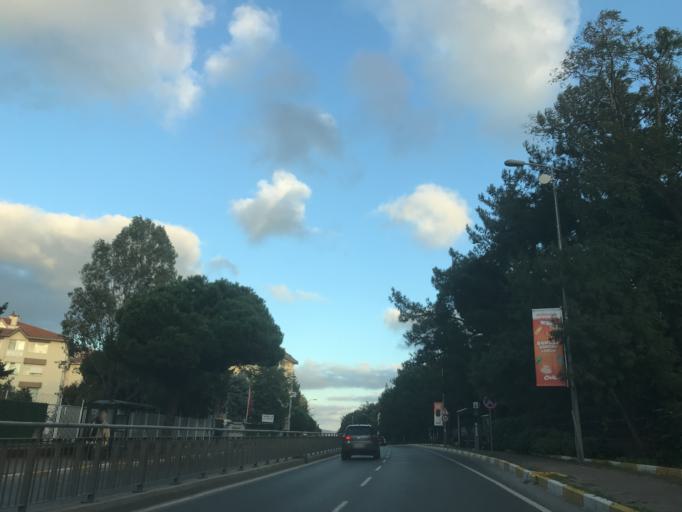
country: TR
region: Istanbul
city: Sisli
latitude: 41.1384
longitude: 29.0340
